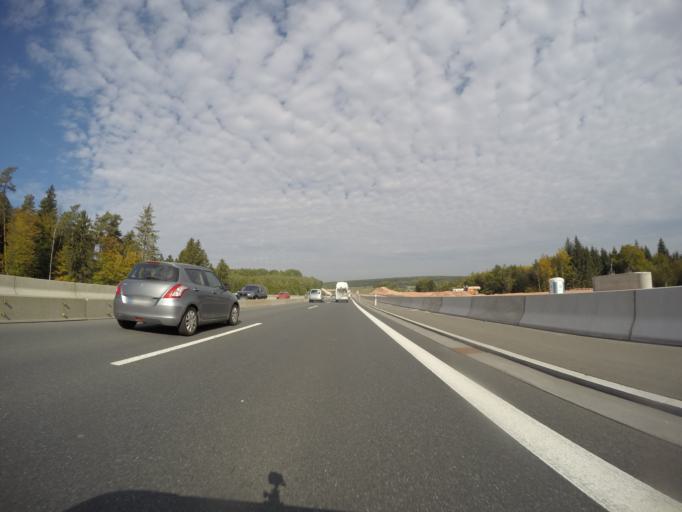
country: DE
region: Bavaria
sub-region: Regierungsbezirk Unterfranken
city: Weibersbrunn
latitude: 49.9267
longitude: 9.3539
